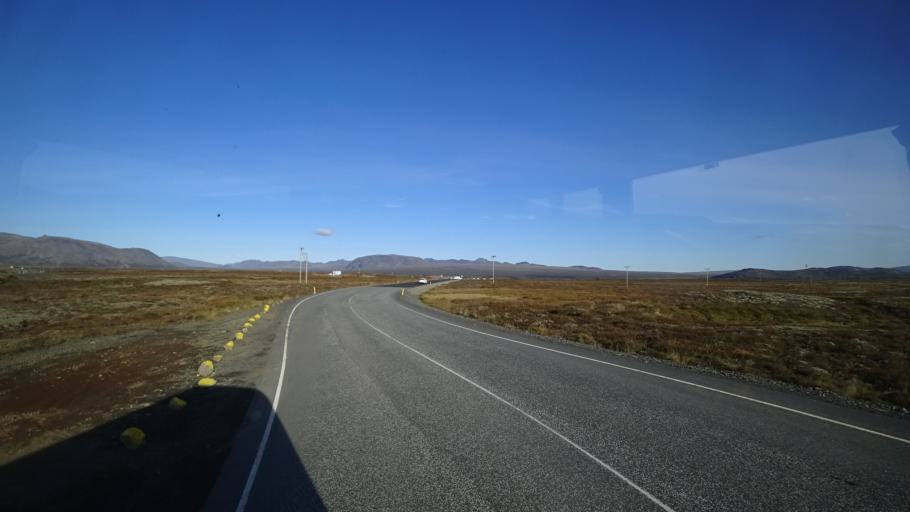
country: IS
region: South
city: Hveragerdi
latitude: 64.2547
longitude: -21.1427
